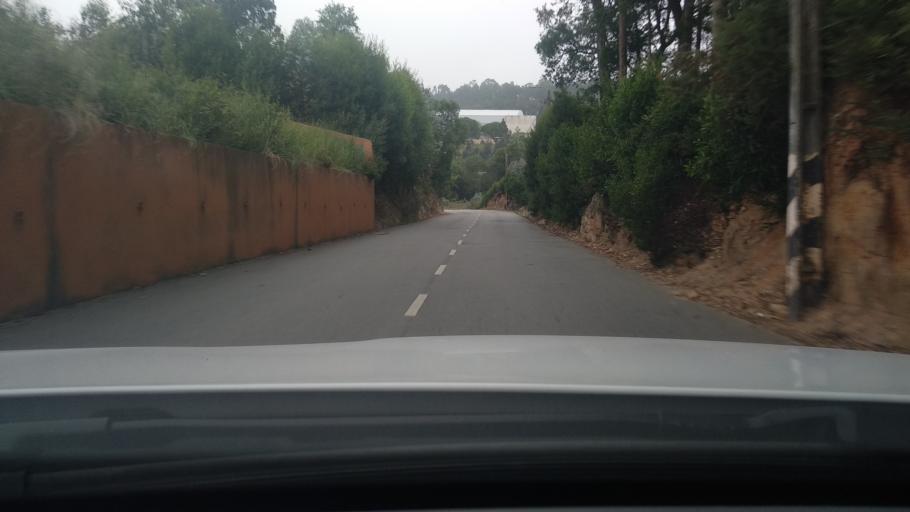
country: PT
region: Aveiro
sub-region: Espinho
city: Silvalde
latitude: 40.9955
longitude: -8.6266
